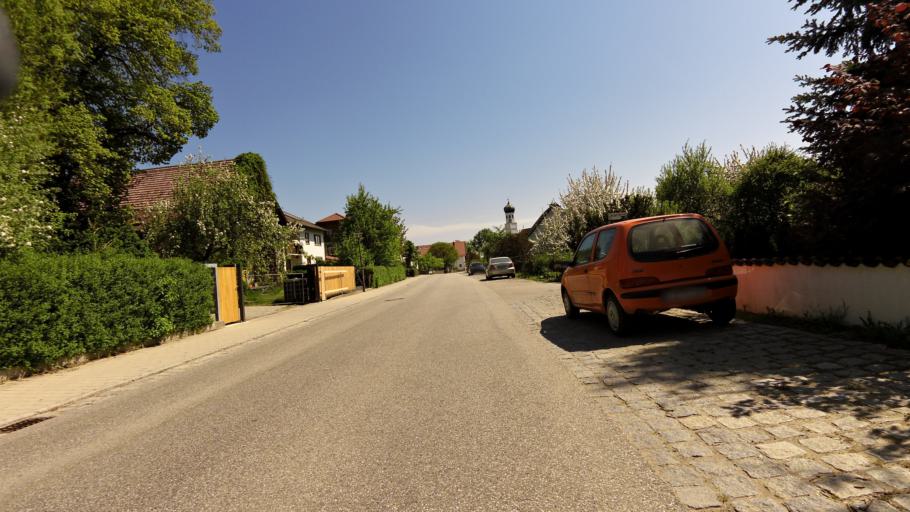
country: DE
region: Bavaria
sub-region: Lower Bavaria
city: Weihmichl
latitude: 48.5749
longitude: 12.0756
